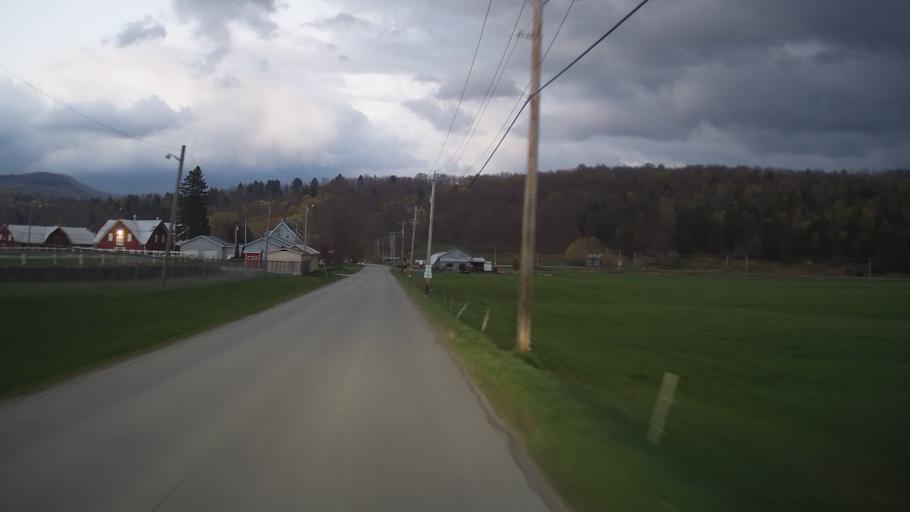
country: US
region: Vermont
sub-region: Orleans County
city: Newport
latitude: 44.7404
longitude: -72.1880
